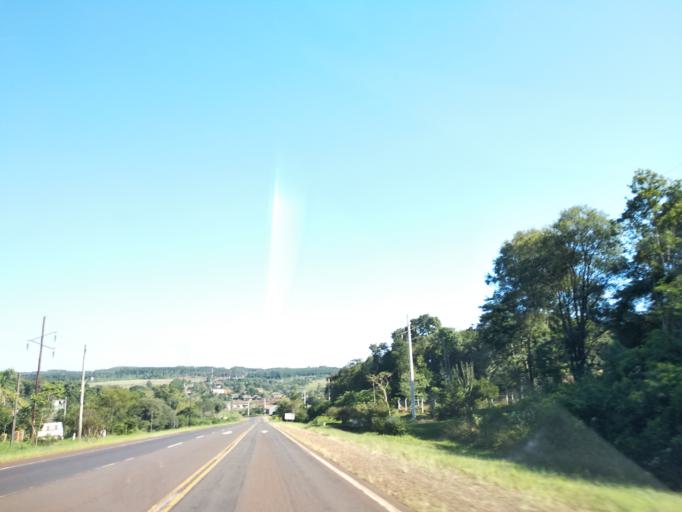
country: AR
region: Misiones
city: Puerto Rico
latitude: -26.8547
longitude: -55.0449
